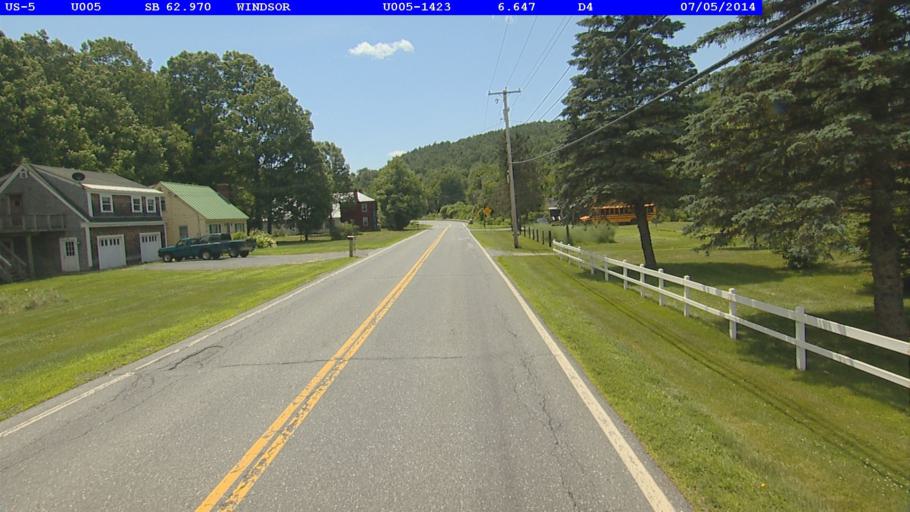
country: US
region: Vermont
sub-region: Windsor County
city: Windsor
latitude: 43.5177
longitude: -72.4031
